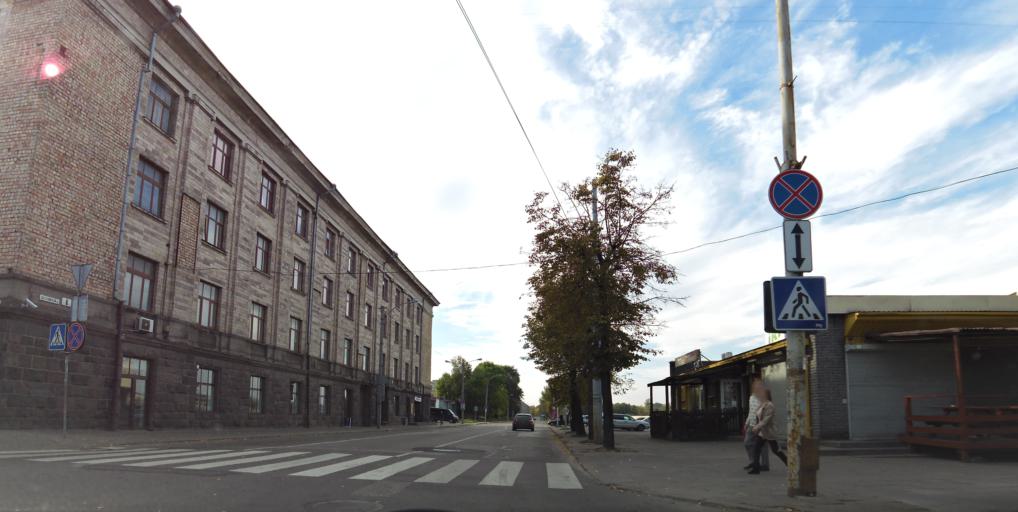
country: LT
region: Vilnius County
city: Naujamiestis
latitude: 54.6704
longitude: 25.2829
